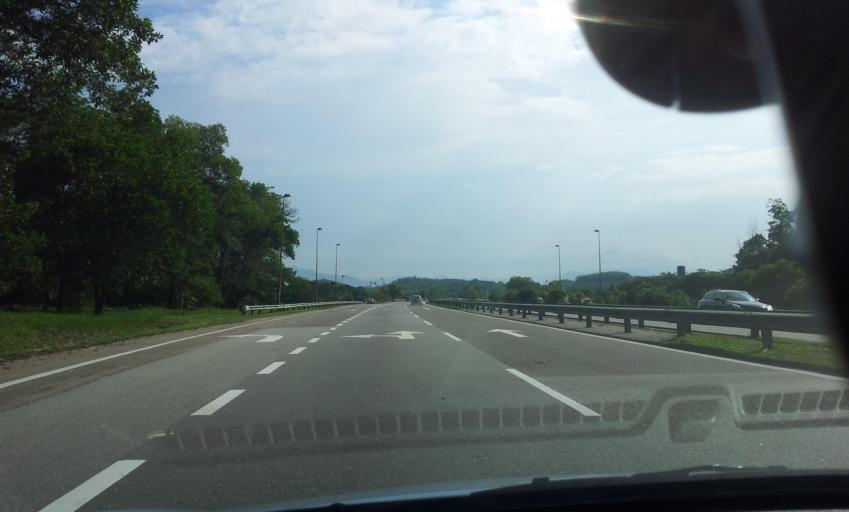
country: MY
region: Pahang
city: Bentong Town
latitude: 3.4960
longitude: 102.1044
